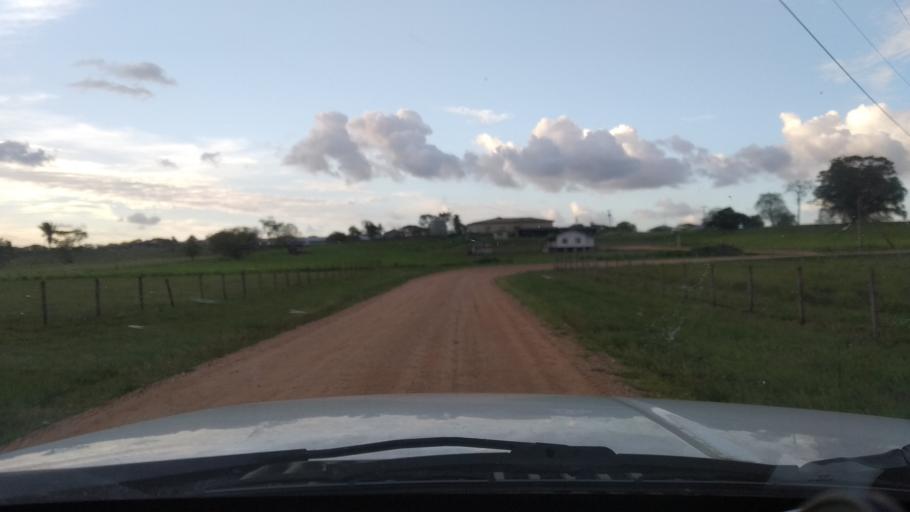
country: BZ
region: Cayo
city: San Ignacio
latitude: 17.2257
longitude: -88.9925
